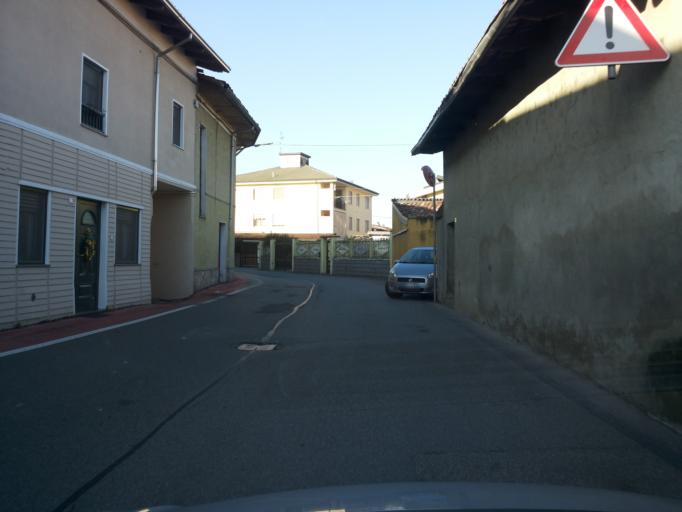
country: IT
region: Piedmont
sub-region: Provincia di Vercelli
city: Cigliano
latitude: 45.3059
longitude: 8.0202
